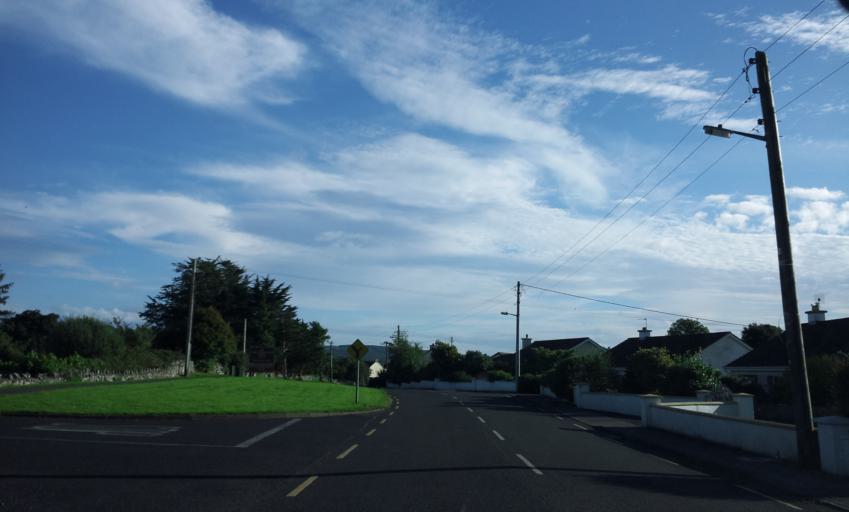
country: IE
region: Munster
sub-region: An Clar
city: Ennis
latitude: 52.9494
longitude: -9.0677
